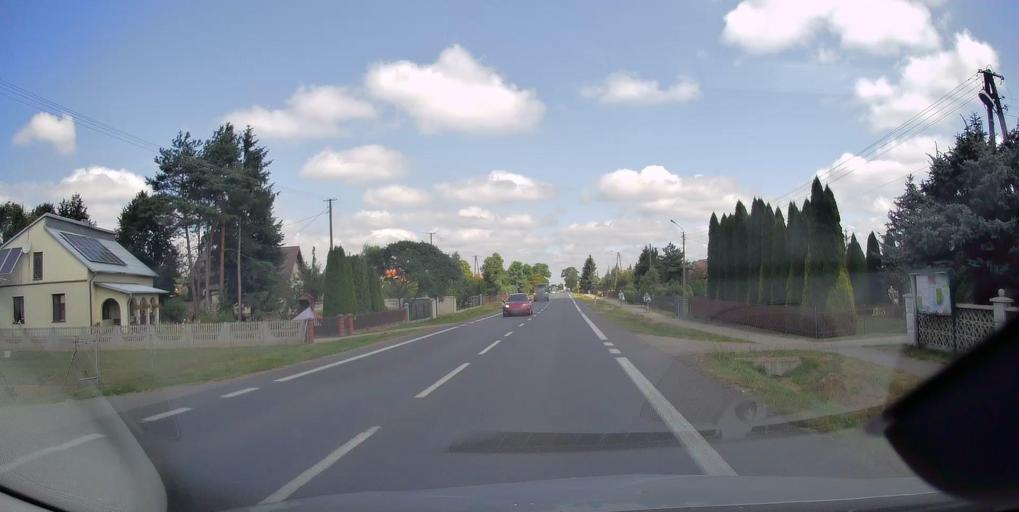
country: PL
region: Subcarpathian Voivodeship
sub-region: Powiat mielecki
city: Przeclaw
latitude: 50.1805
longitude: 21.4964
